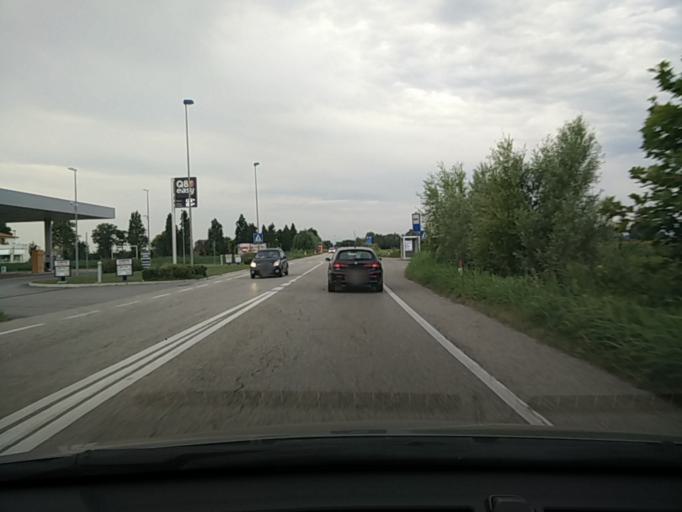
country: IT
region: Veneto
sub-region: Provincia di Venezia
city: Passarella
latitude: 45.5583
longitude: 12.5768
